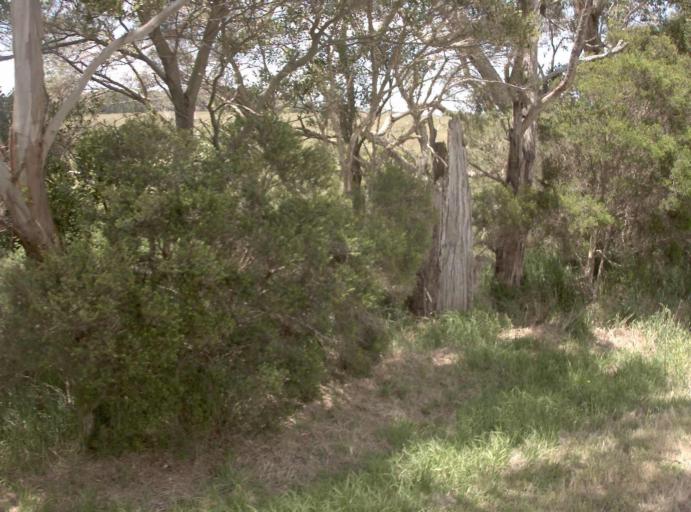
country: AU
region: Victoria
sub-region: Bass Coast
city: North Wonthaggi
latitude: -38.6600
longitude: 146.0184
